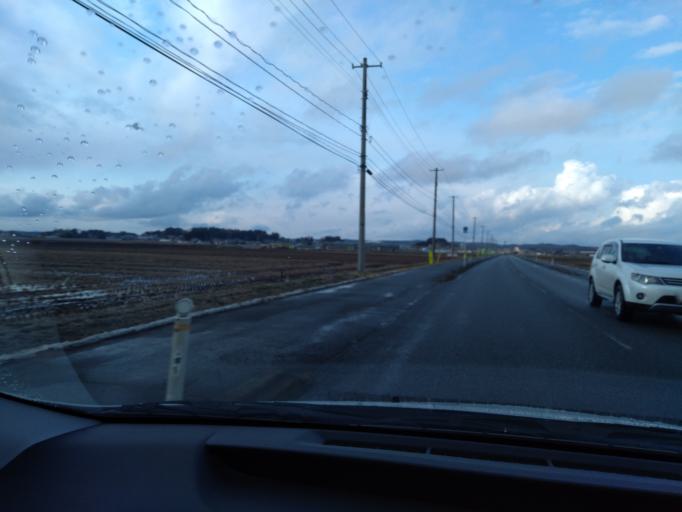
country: JP
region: Iwate
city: Ichinoseki
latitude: 38.7617
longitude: 141.1169
